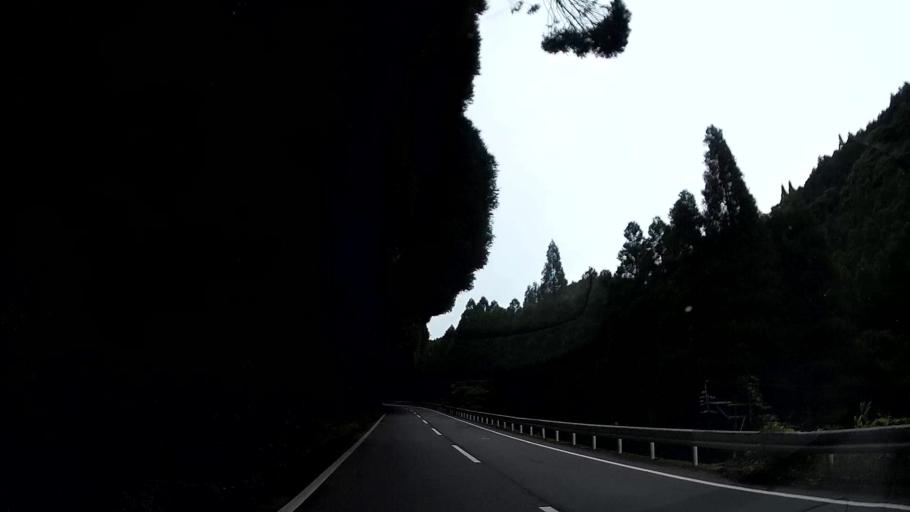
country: JP
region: Kumamoto
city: Kikuchi
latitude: 33.0394
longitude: 130.8934
